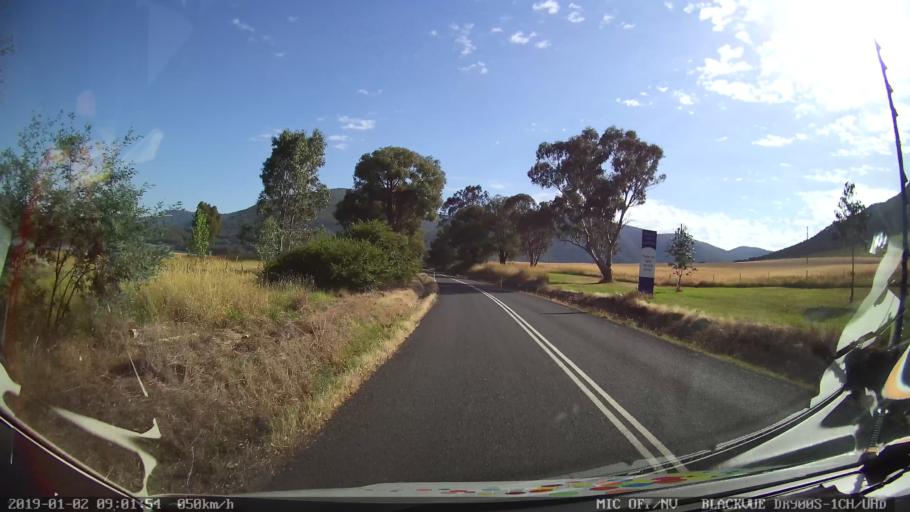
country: AU
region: New South Wales
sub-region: Tumut Shire
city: Tumut
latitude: -35.5771
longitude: 148.3098
